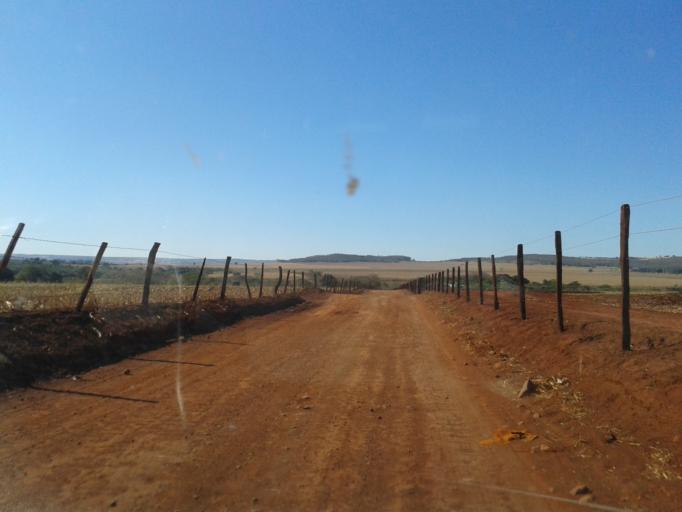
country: BR
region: Minas Gerais
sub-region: Centralina
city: Centralina
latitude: -18.5860
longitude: -49.1855
